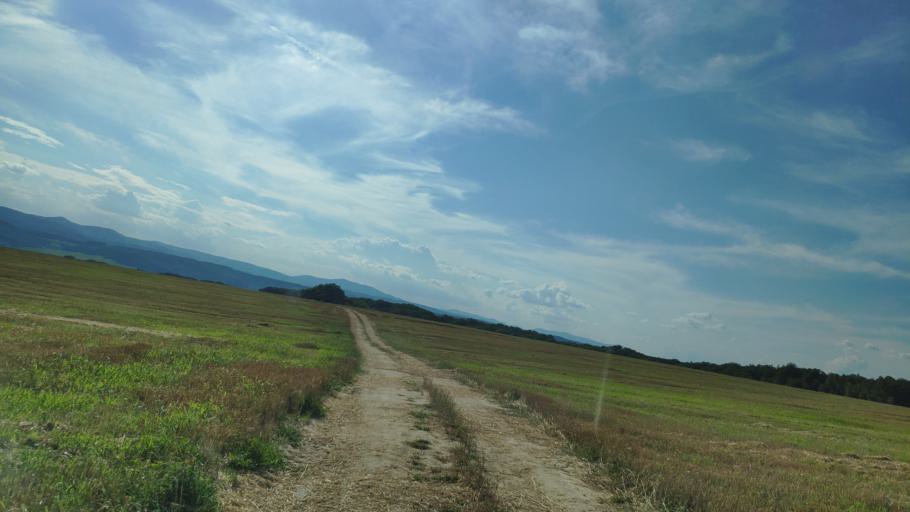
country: SK
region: Presovsky
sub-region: Okres Presov
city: Presov
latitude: 48.9171
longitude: 21.2988
